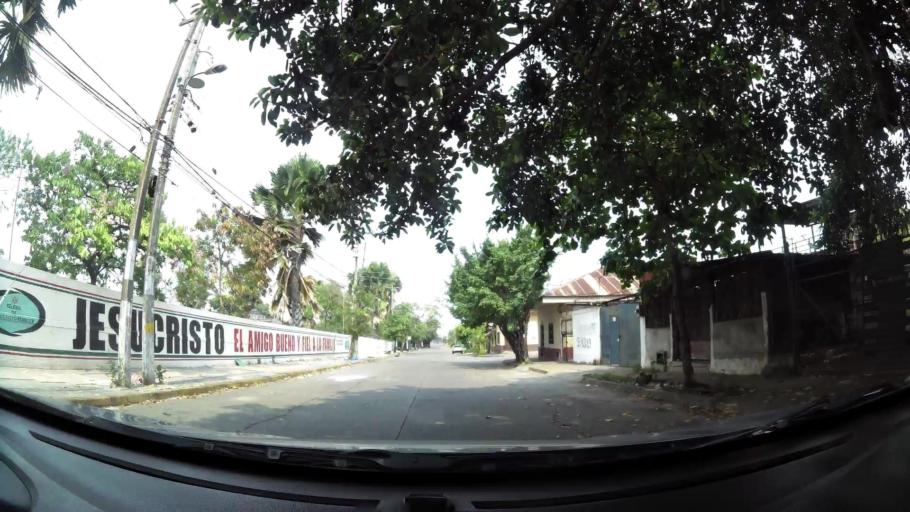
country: HN
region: Cortes
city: San Pedro Sula
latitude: 15.4933
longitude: -88.0289
